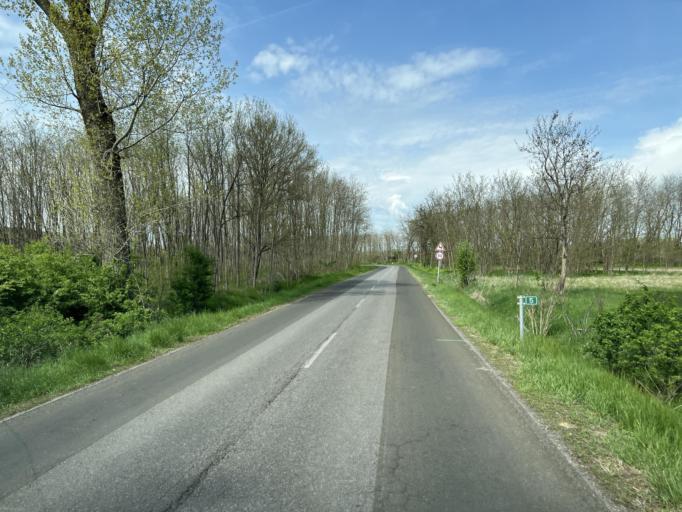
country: HU
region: Pest
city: Albertirsa
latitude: 47.2086
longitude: 19.6125
